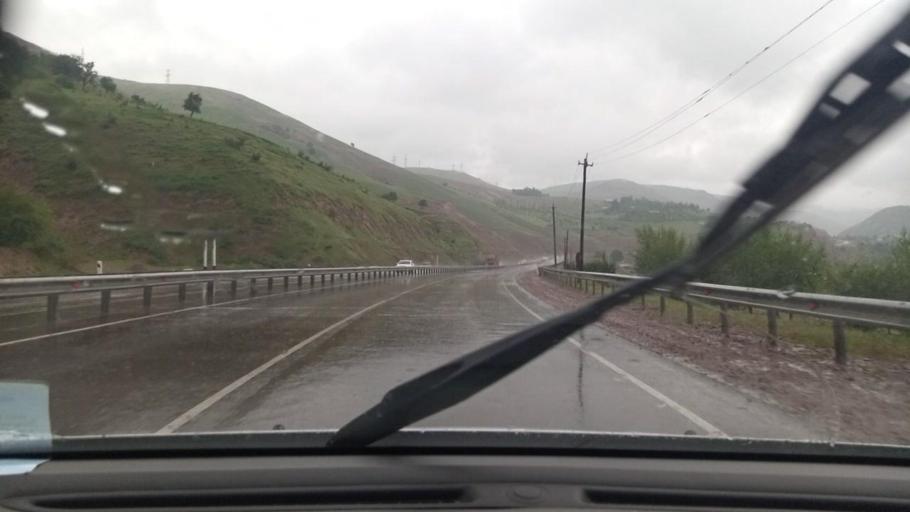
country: UZ
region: Toshkent
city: Angren
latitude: 41.0921
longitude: 70.3197
